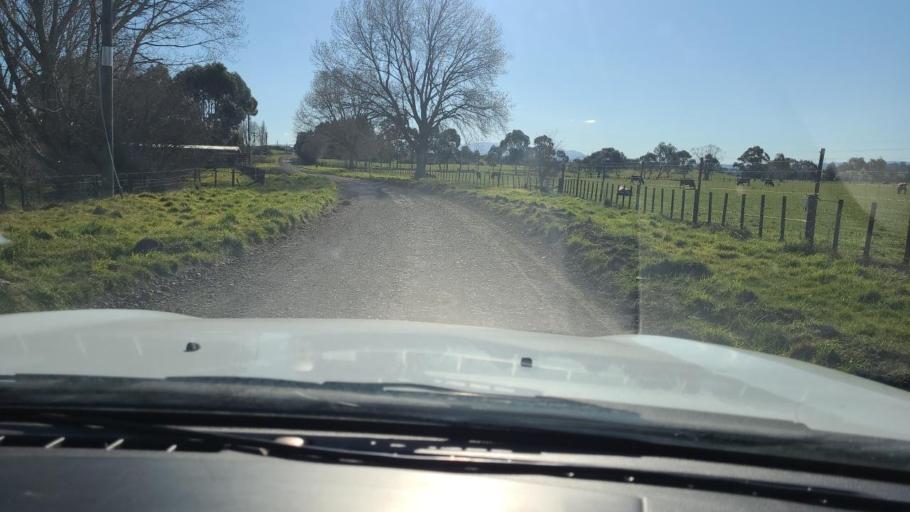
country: NZ
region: Hawke's Bay
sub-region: Napier City
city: Taradale
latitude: -39.4608
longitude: 176.6362
